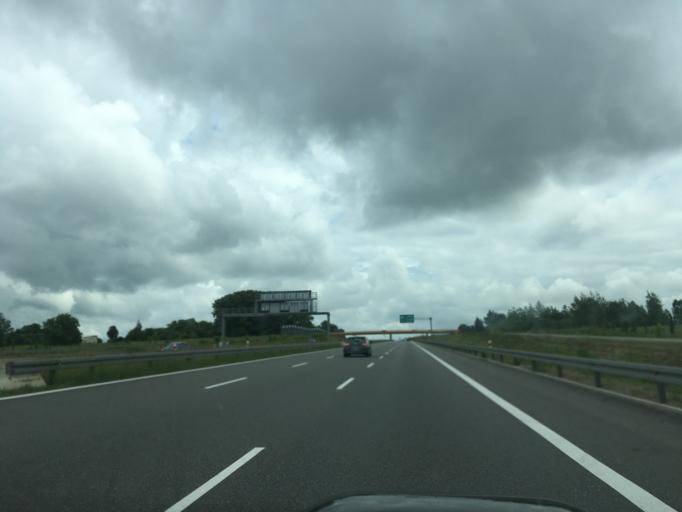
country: PL
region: Lublin Voivodeship
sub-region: Powiat lubelski
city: Lublin
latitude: 51.2978
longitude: 22.5352
